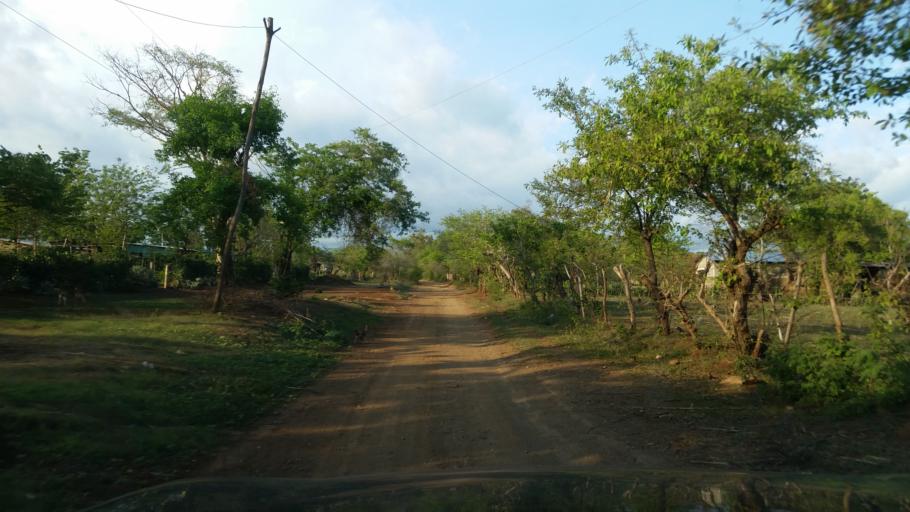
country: NI
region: Managua
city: Masachapa
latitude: 11.7781
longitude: -86.4770
